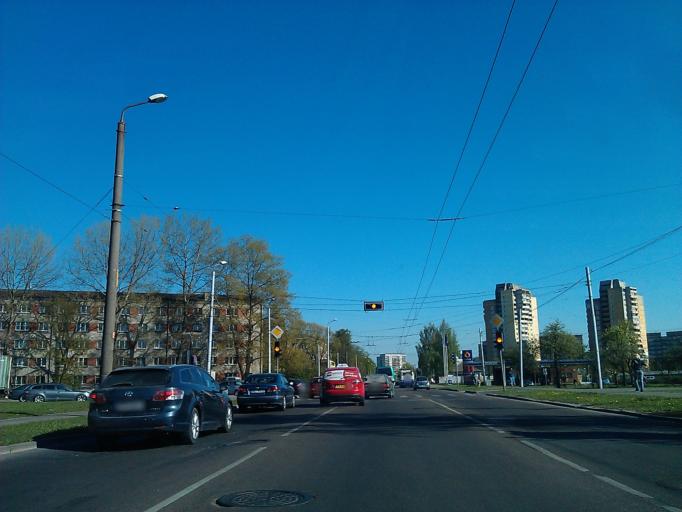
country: LV
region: Riga
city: Riga
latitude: 56.9642
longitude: 24.1677
